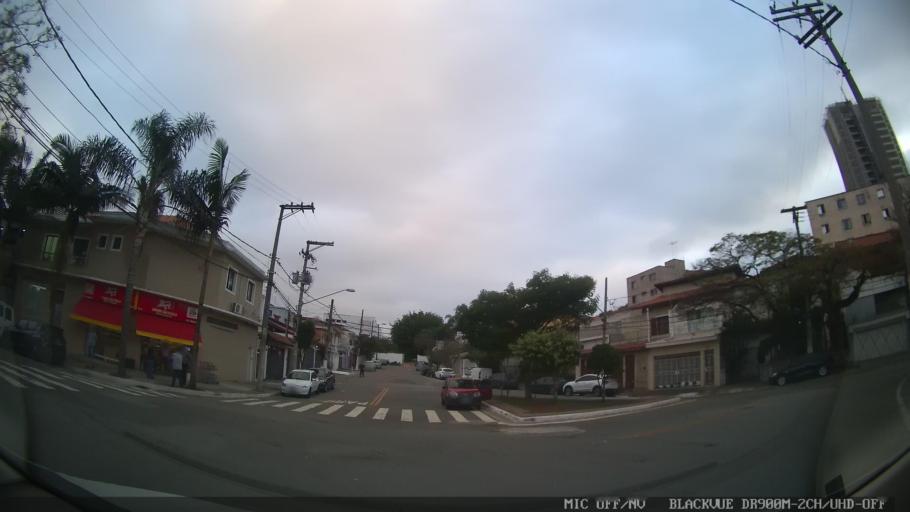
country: BR
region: Sao Paulo
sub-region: Sao Paulo
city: Sao Paulo
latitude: -23.4922
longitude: -46.6188
